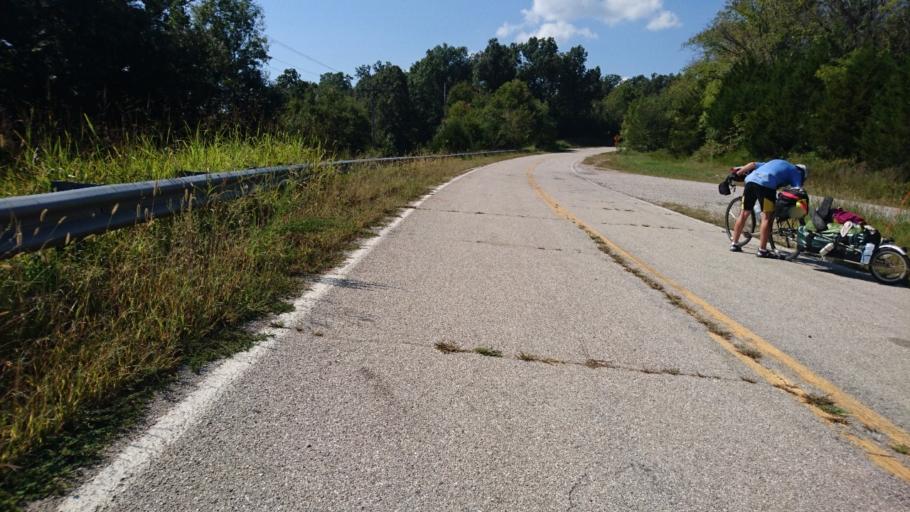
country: US
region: Missouri
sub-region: Pulaski County
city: Richland
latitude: 37.7585
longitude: -92.4528
